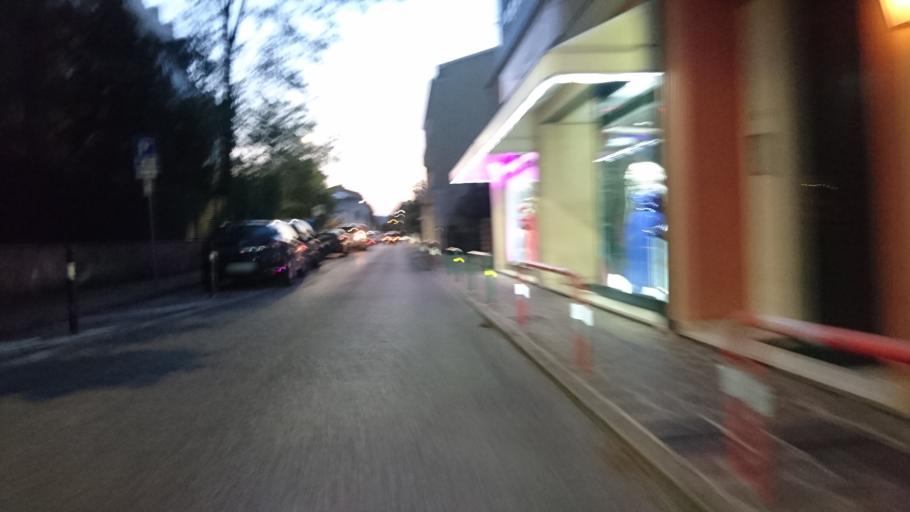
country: IT
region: Veneto
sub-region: Provincia di Padova
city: Abano Terme
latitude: 45.3502
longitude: 11.7786
